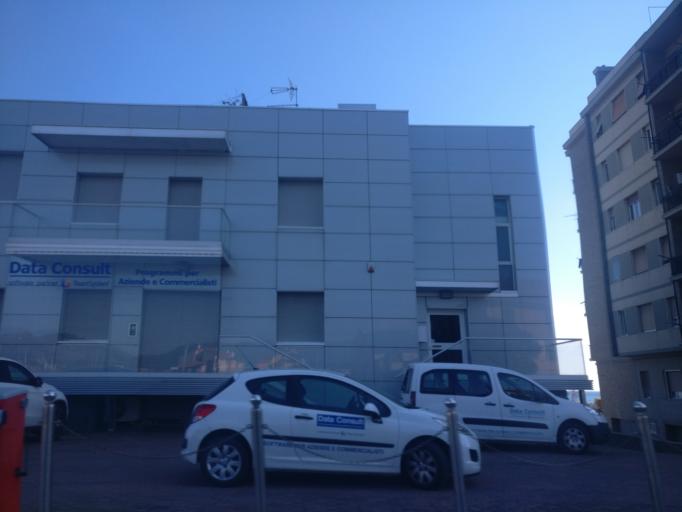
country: IT
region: Liguria
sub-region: Provincia di Savona
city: Valleggia
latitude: 44.2810
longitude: 8.4435
